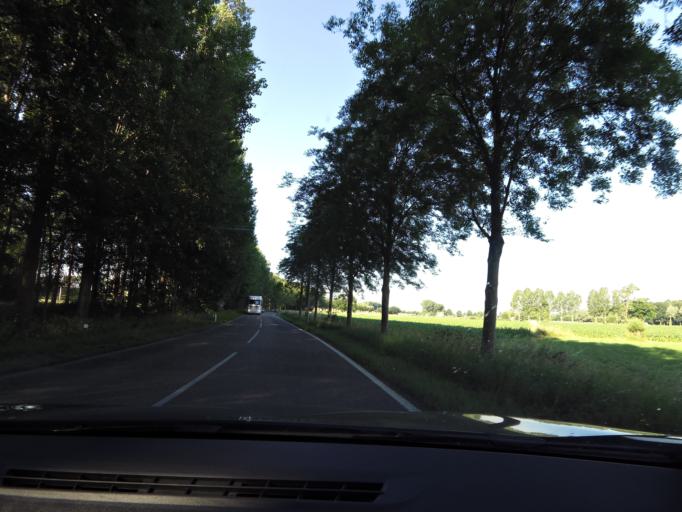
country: NL
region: Gelderland
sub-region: Gemeente Voorst
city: Wilp
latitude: 52.2193
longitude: 6.1238
